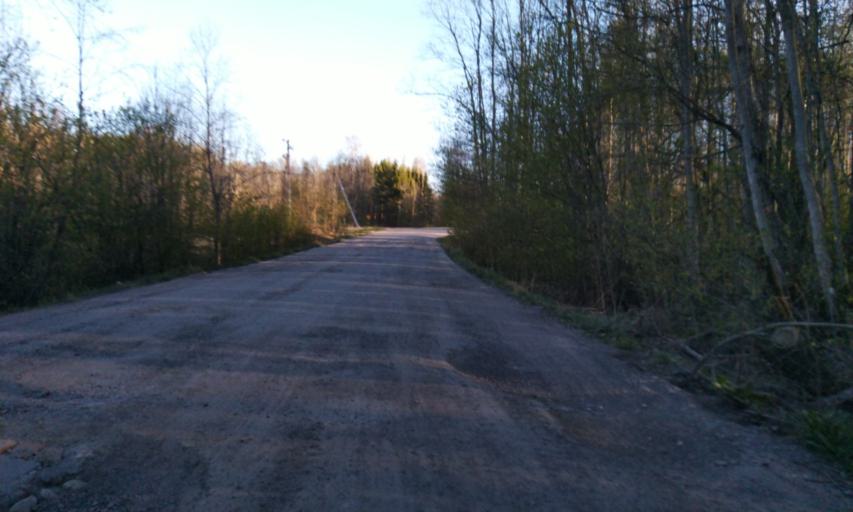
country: RU
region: Leningrad
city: Toksovo
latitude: 60.1391
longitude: 30.5704
